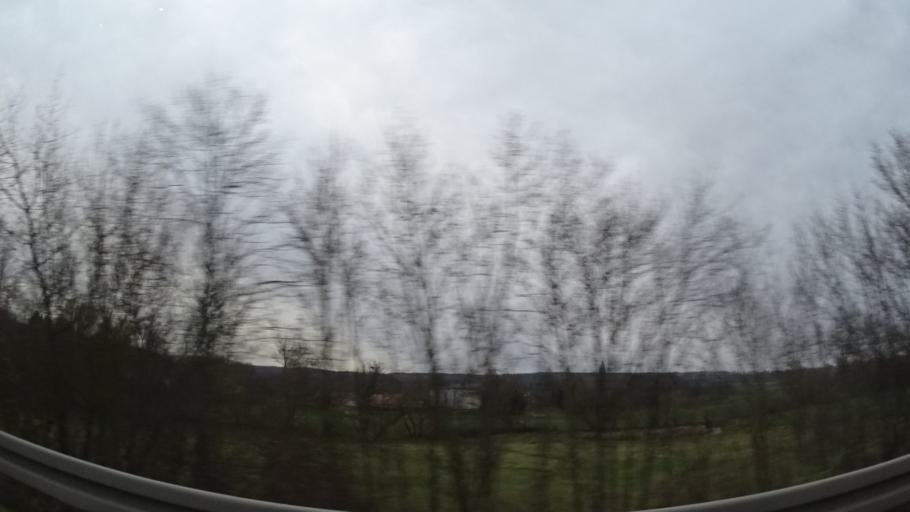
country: DE
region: Hesse
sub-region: Regierungsbezirk Kassel
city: Hunfeld
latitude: 50.6818
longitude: 9.7533
